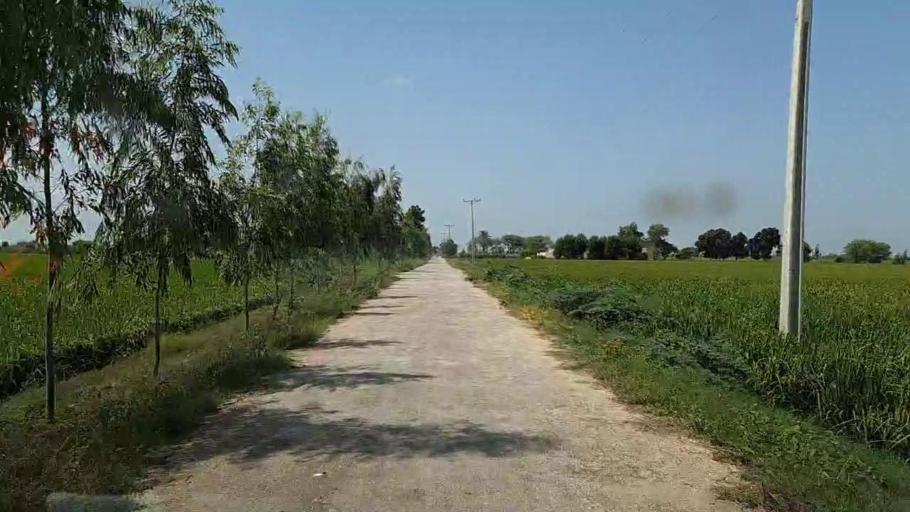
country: PK
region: Sindh
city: Kario
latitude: 24.6286
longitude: 68.5344
